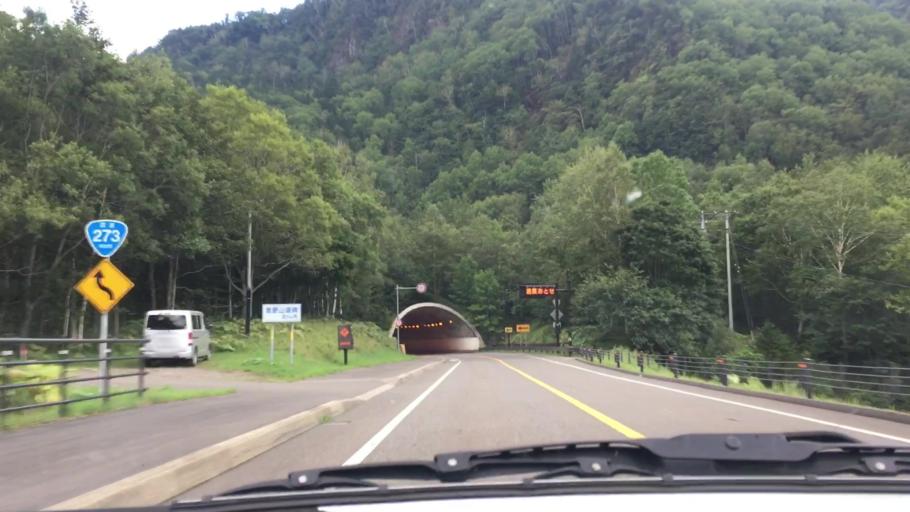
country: JP
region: Hokkaido
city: Otofuke
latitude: 43.3637
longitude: 143.2355
